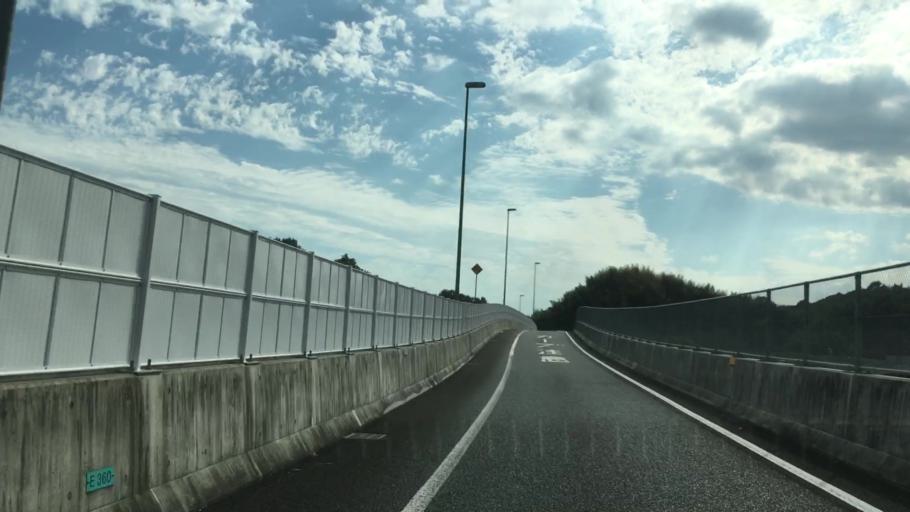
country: JP
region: Hiroshima
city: Hatsukaichi
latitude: 34.3481
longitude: 132.3184
